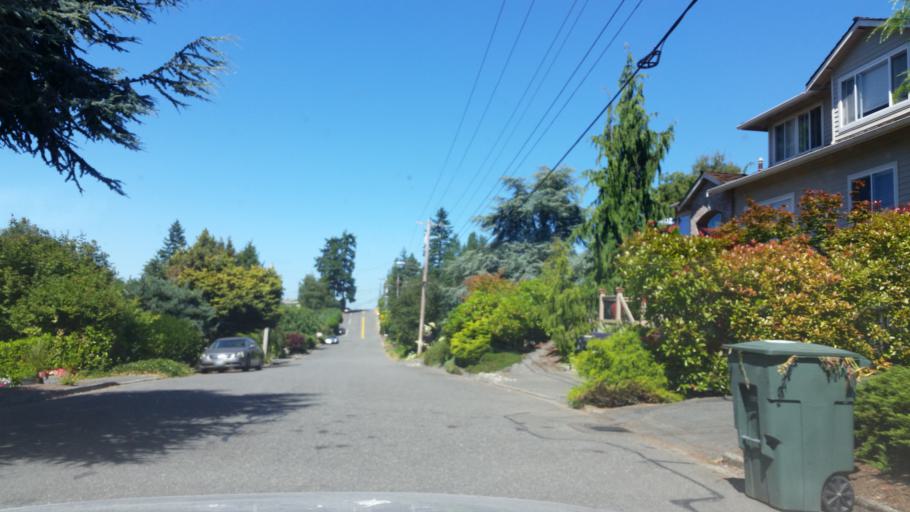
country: US
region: Washington
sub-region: Snohomish County
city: Edmonds
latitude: 47.8036
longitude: -122.3722
